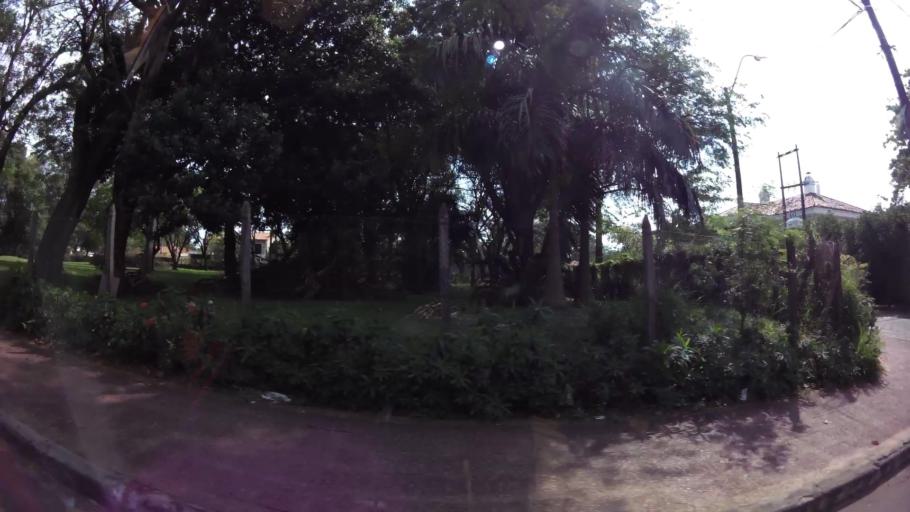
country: PY
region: Central
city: Fernando de la Mora
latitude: -25.2708
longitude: -57.5616
